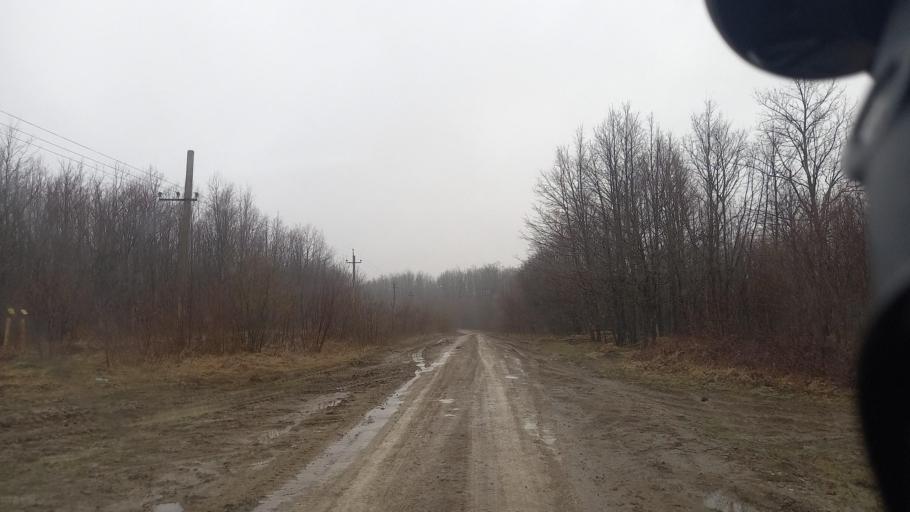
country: RU
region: Krasnodarskiy
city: Saratovskaya
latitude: 44.6320
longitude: 39.2595
